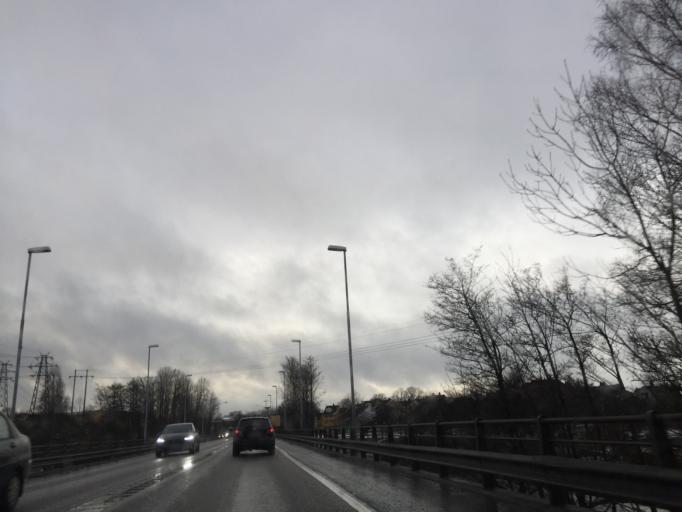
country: NO
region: Ostfold
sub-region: Moss
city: Moss
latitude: 59.4387
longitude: 10.6746
